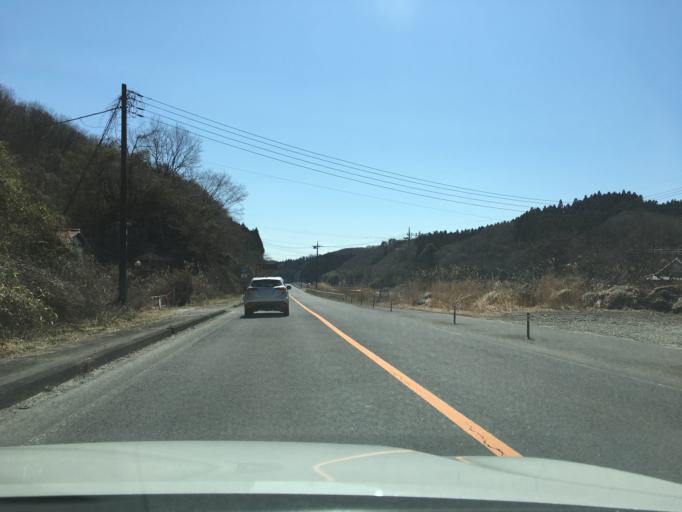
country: JP
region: Tochigi
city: Kuroiso
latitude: 37.0484
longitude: 140.1705
